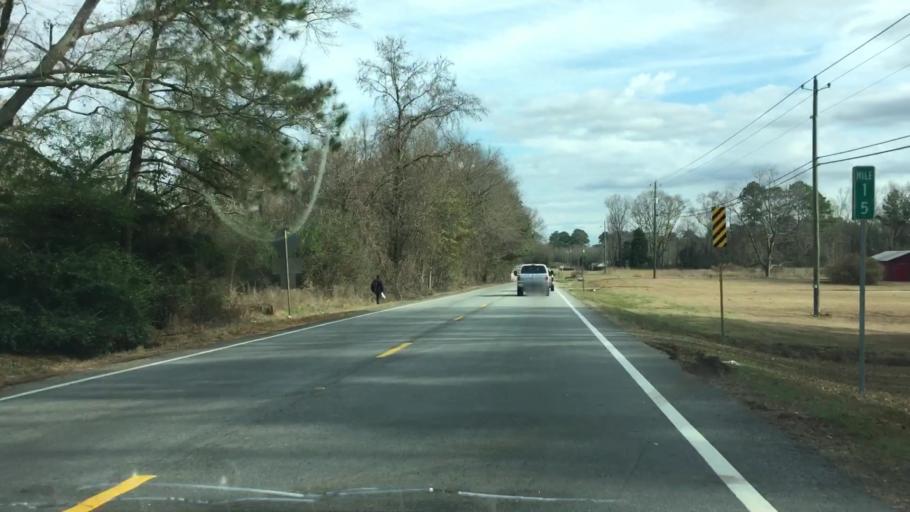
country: US
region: Georgia
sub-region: Henry County
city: McDonough
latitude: 33.4278
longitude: -84.0851
